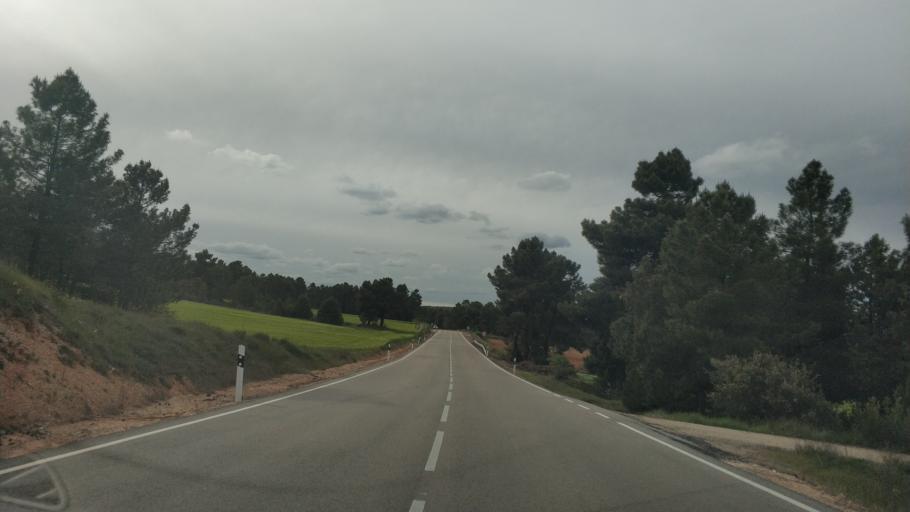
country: ES
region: Castille and Leon
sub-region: Provincia de Soria
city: Valdenebro
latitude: 41.5541
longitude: -2.9640
